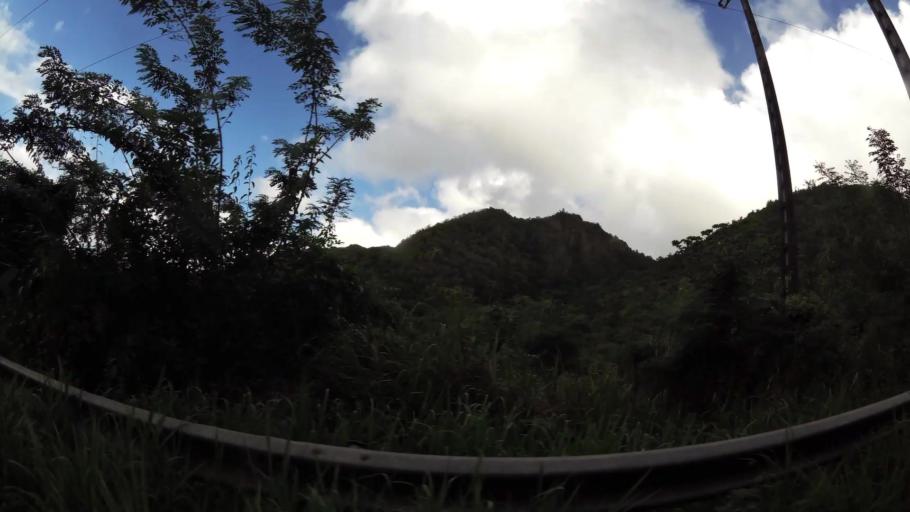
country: MQ
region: Martinique
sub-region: Martinique
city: Les Trois-Ilets
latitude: 14.5093
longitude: -61.0784
